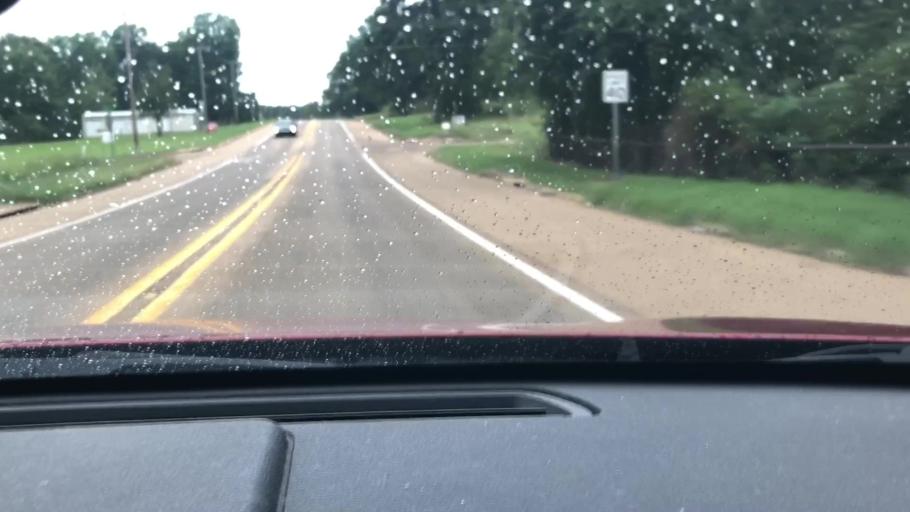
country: US
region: Arkansas
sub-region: Lafayette County
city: Stamps
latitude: 33.3585
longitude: -93.4366
